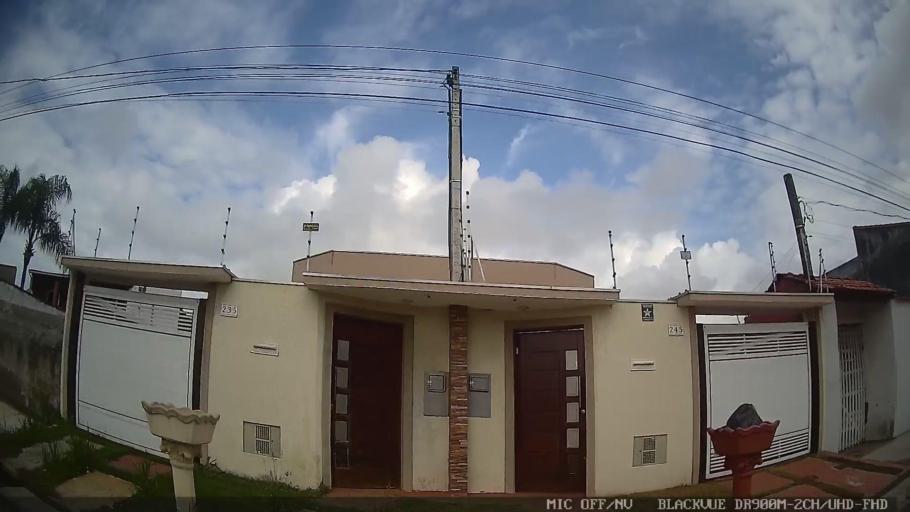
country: BR
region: Sao Paulo
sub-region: Itanhaem
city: Itanhaem
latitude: -24.1972
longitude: -46.8227
